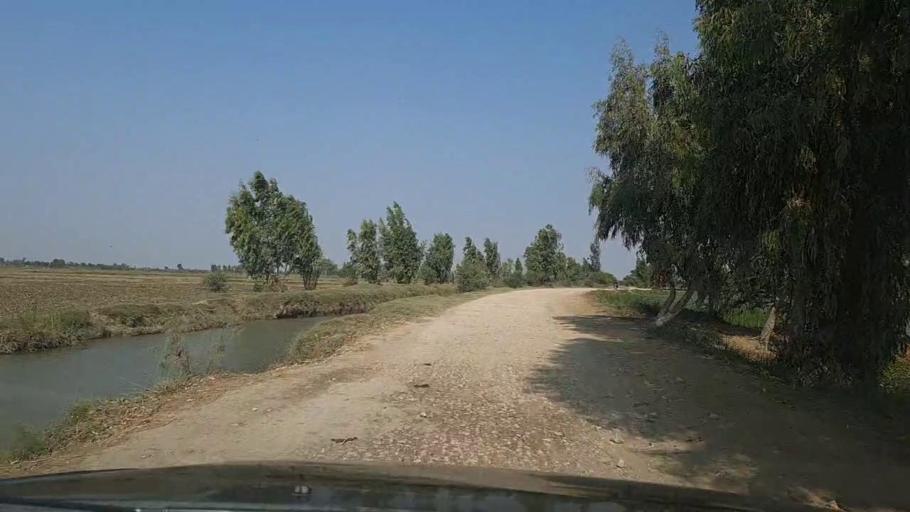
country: PK
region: Sindh
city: Thatta
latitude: 24.6233
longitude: 67.8140
